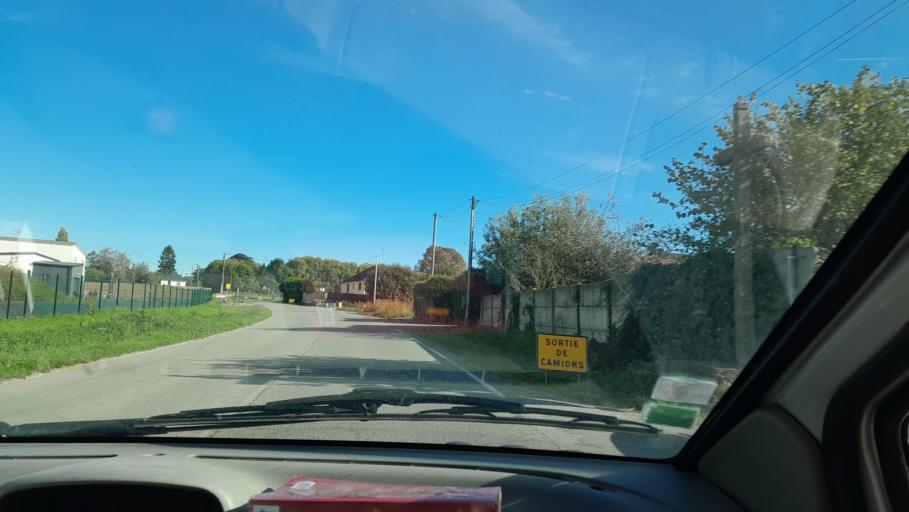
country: FR
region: Brittany
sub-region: Departement d'Ille-et-Vilaine
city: Etrelles
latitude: 48.0573
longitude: -1.1845
